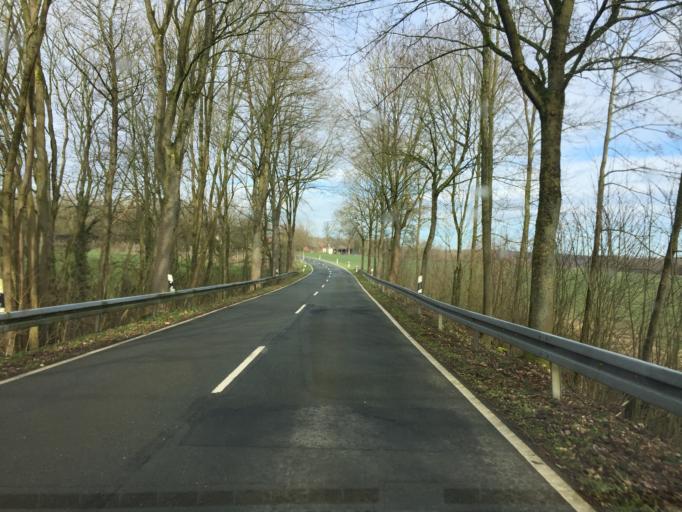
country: DE
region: Lower Saxony
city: Aerzen
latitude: 52.0767
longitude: 9.1890
